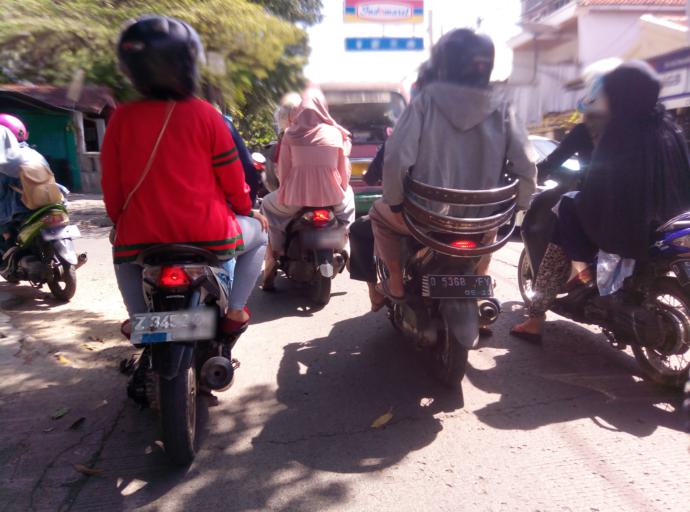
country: ID
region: West Java
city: Bandung
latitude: -6.8937
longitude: 107.6383
